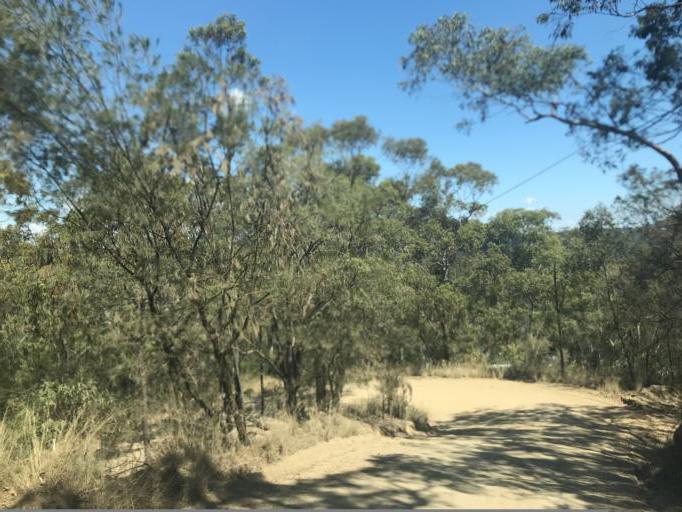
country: AU
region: New South Wales
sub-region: Hawkesbury
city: Pitt Town
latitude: -33.4140
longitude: 150.9209
